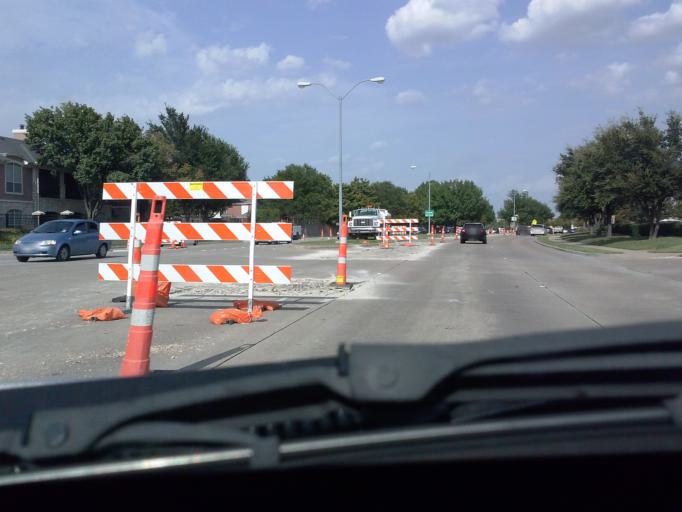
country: US
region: Texas
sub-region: Denton County
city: The Colony
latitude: 33.0453
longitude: -96.8258
